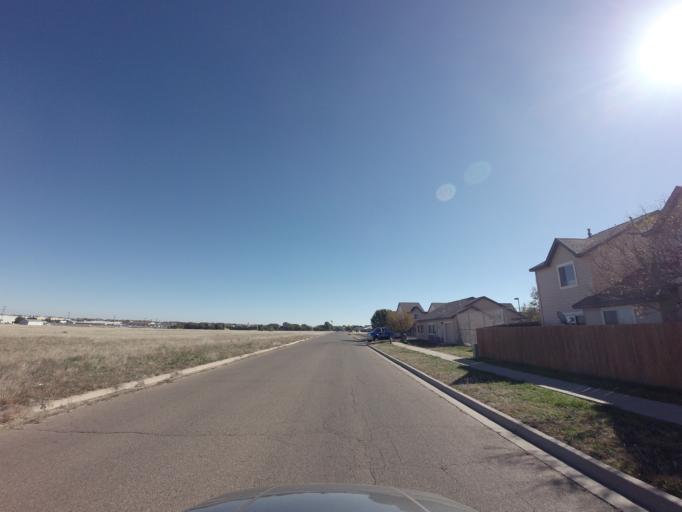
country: US
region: New Mexico
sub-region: Curry County
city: Clovis
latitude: 34.4310
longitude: -103.2071
